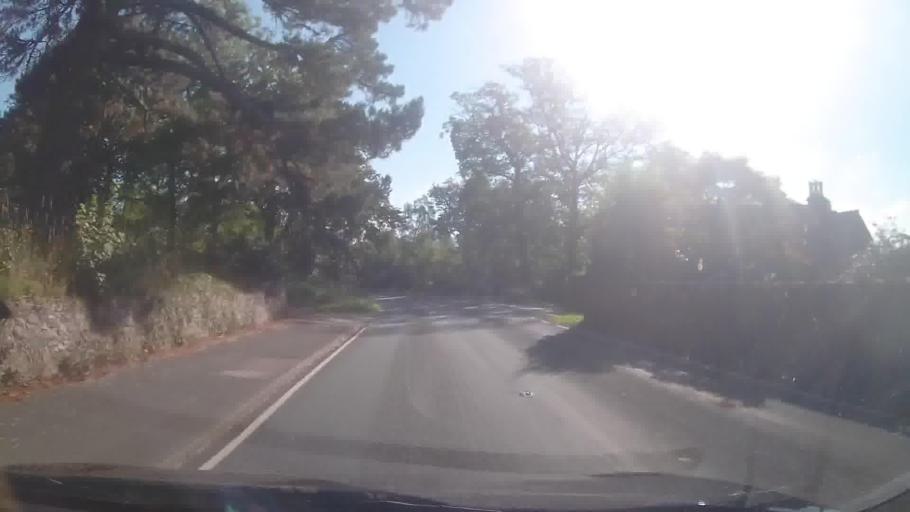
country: GB
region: England
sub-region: Cumbria
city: Seascale
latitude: 54.3580
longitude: -3.3824
